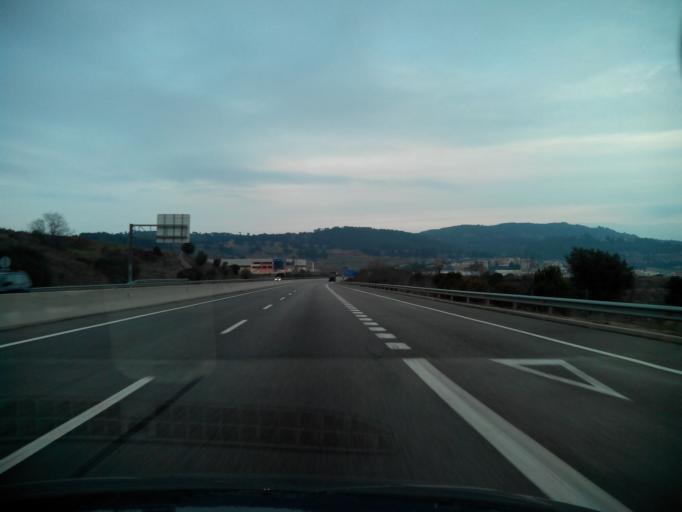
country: ES
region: Catalonia
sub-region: Provincia de Barcelona
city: Navas
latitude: 41.8904
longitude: 1.8744
